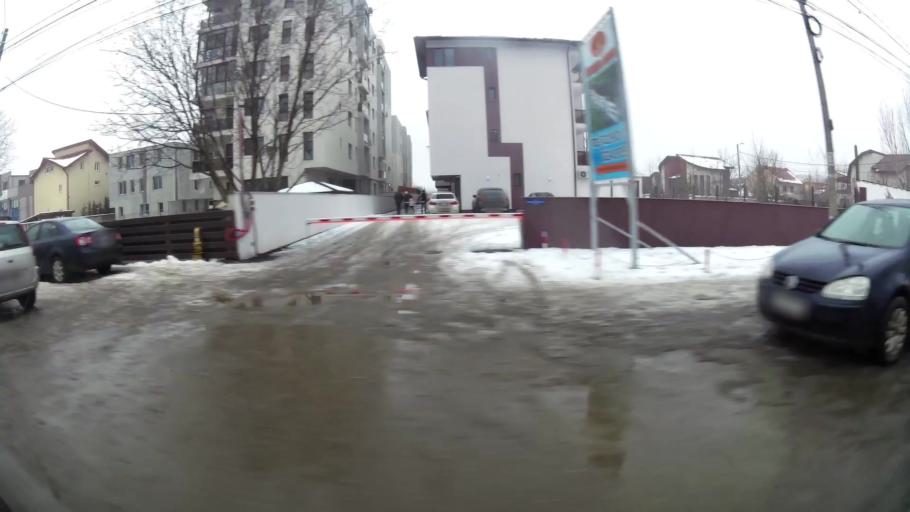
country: RO
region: Ilfov
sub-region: Comuna Chiajna
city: Rosu
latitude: 44.4100
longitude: 26.0011
